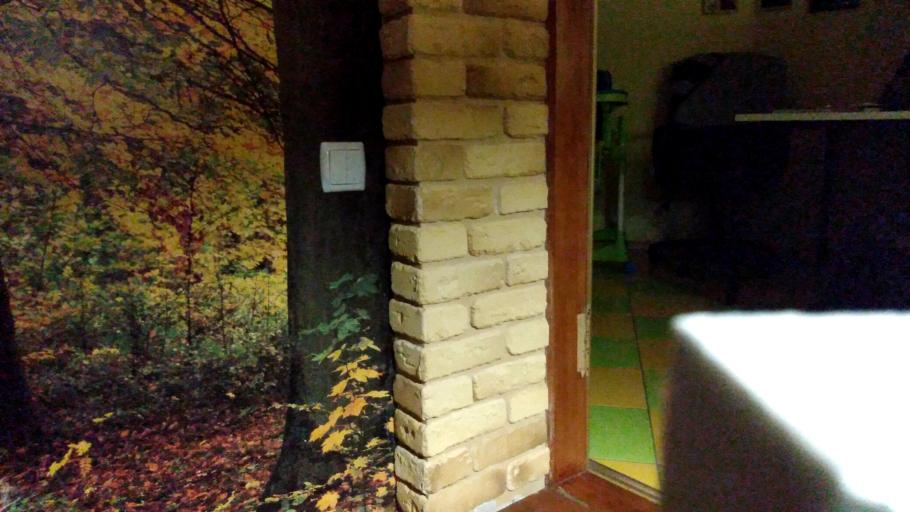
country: RU
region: Vologda
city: Lipin Bor
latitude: 60.8797
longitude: 38.0044
